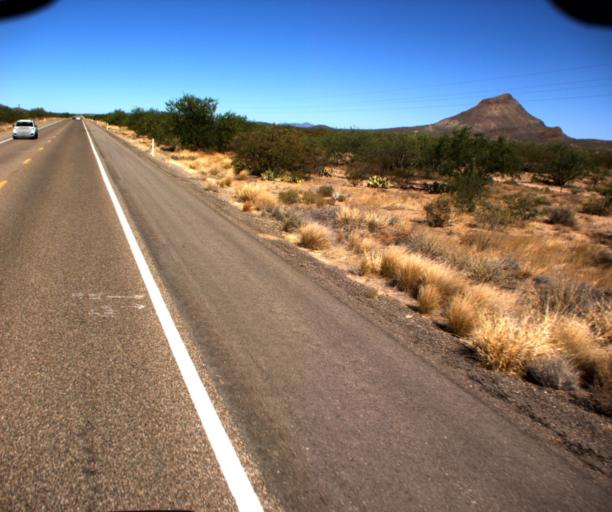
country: US
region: Arizona
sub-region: Pima County
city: Three Points
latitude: 32.0410
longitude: -111.4579
